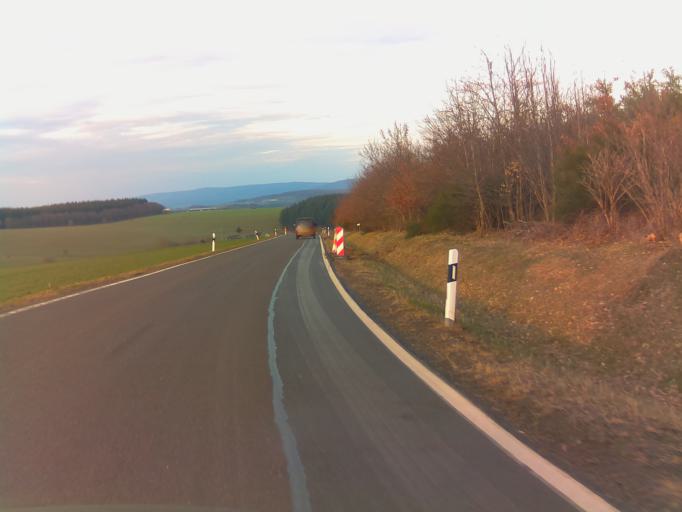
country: DE
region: Rheinland-Pfalz
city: Sulzbach
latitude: 49.8400
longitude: 7.3411
